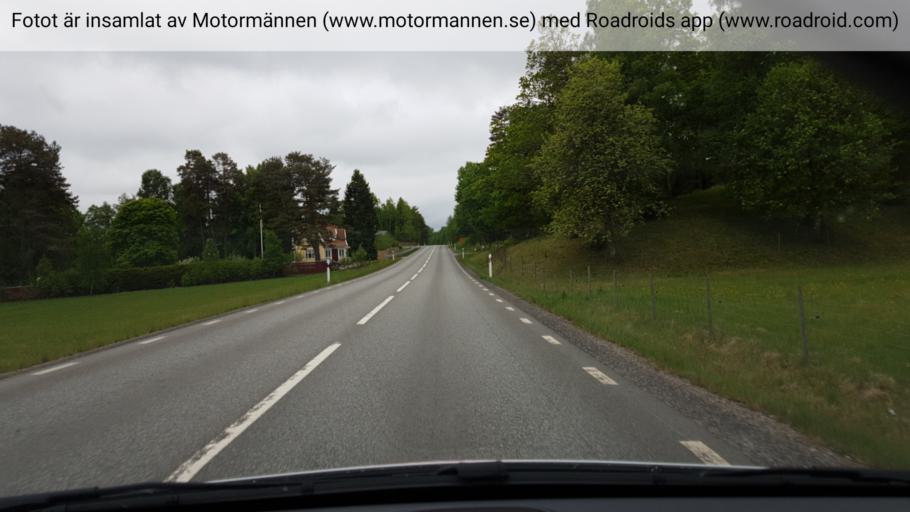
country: SE
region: Joenkoeping
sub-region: Mullsjo Kommun
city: Mullsjoe
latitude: 57.8138
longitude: 13.8525
